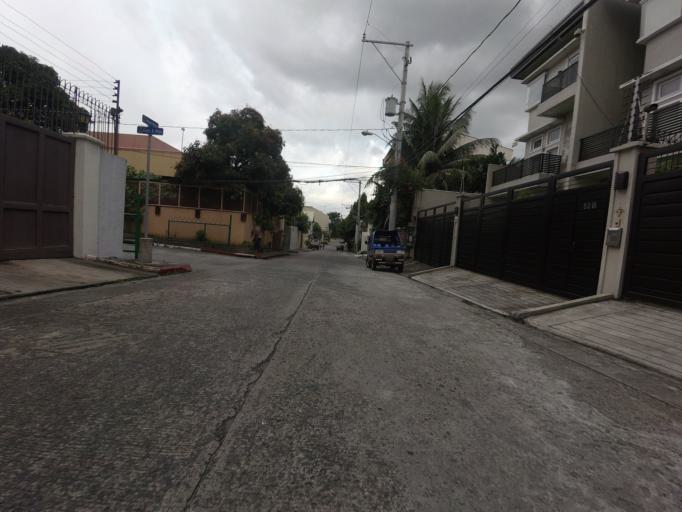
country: PH
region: Metro Manila
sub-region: Mandaluyong
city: Mandaluyong City
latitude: 14.5932
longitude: 121.0418
